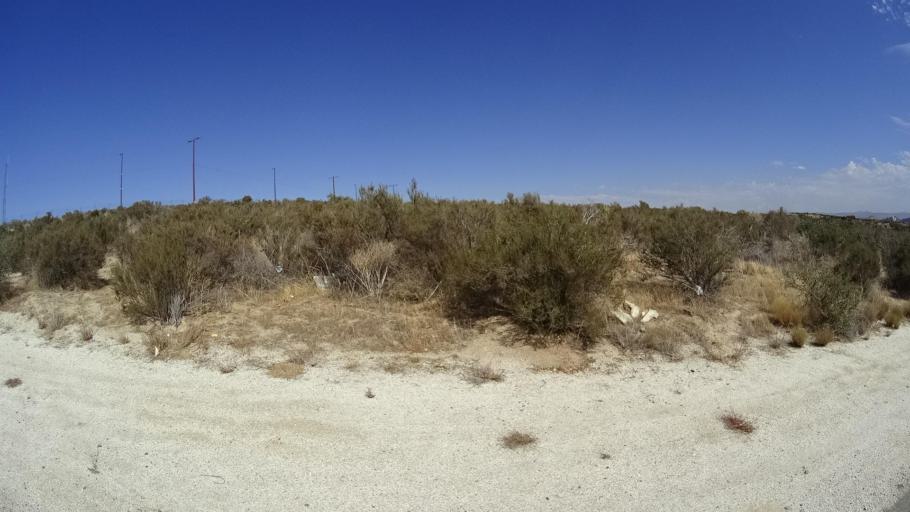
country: US
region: California
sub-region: San Diego County
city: Campo
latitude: 32.6799
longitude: -116.2922
